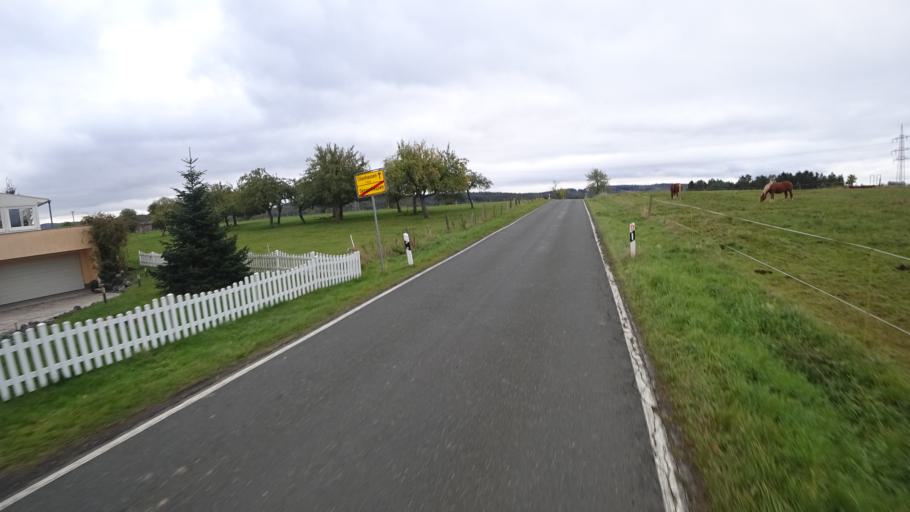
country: DE
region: Rheinland-Pfalz
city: Oberhaid
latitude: 50.5247
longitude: 7.7171
